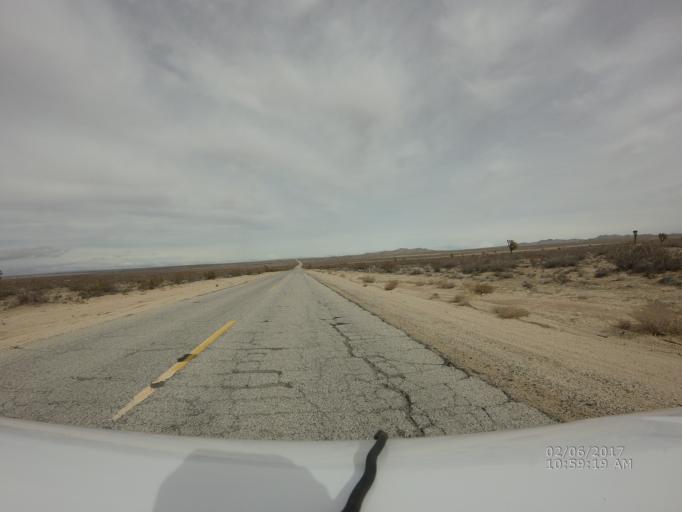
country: US
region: California
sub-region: Los Angeles County
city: Lake Los Angeles
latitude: 34.6371
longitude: -117.7026
